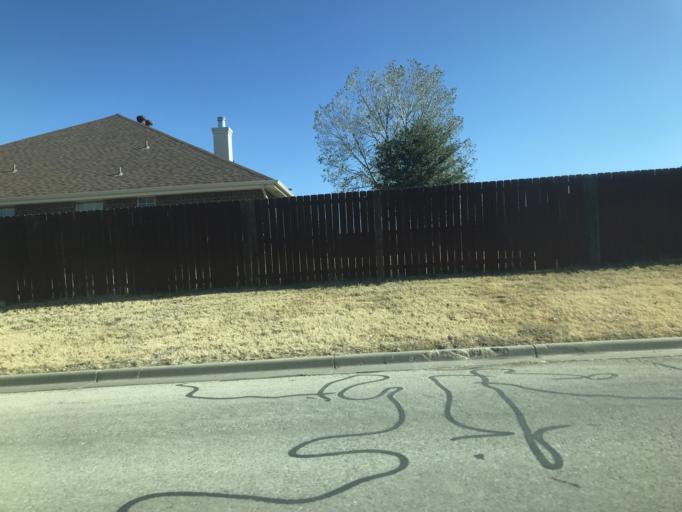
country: US
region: Texas
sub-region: Taylor County
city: Abilene
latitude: 32.4914
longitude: -99.6894
